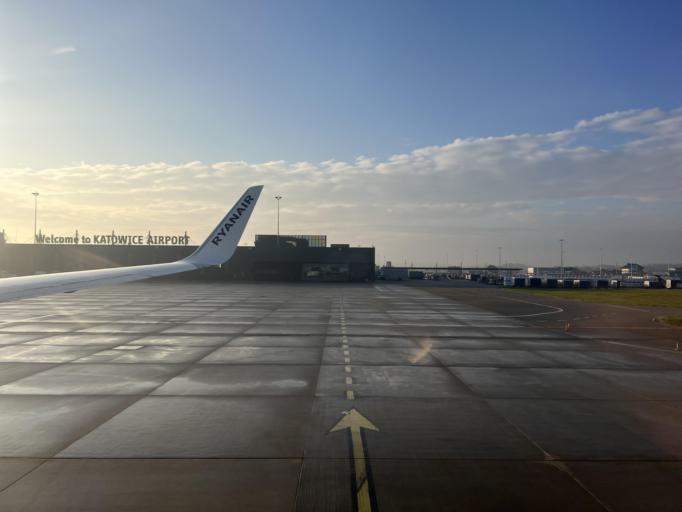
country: PL
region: Silesian Voivodeship
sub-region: Powiat tarnogorski
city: Ozarowice
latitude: 50.4724
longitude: 19.0689
